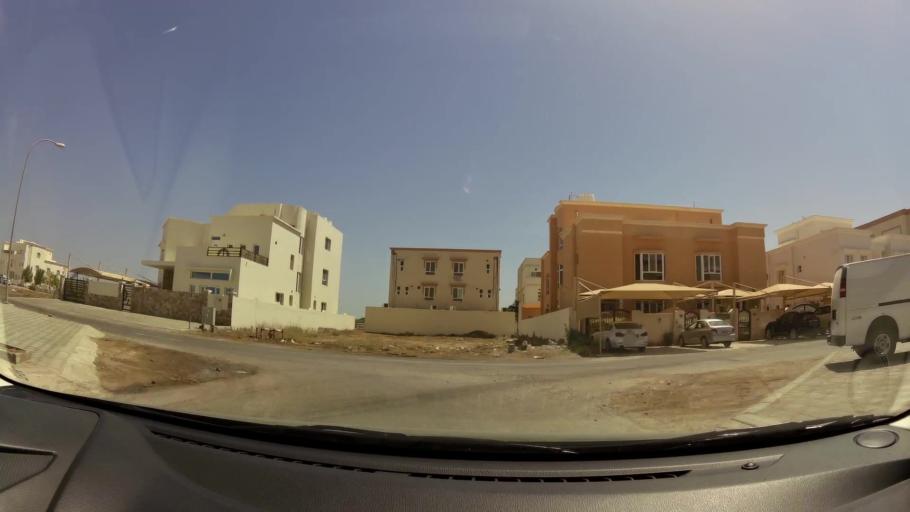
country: OM
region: Muhafazat Masqat
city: As Sib al Jadidah
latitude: 23.6228
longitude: 58.2594
